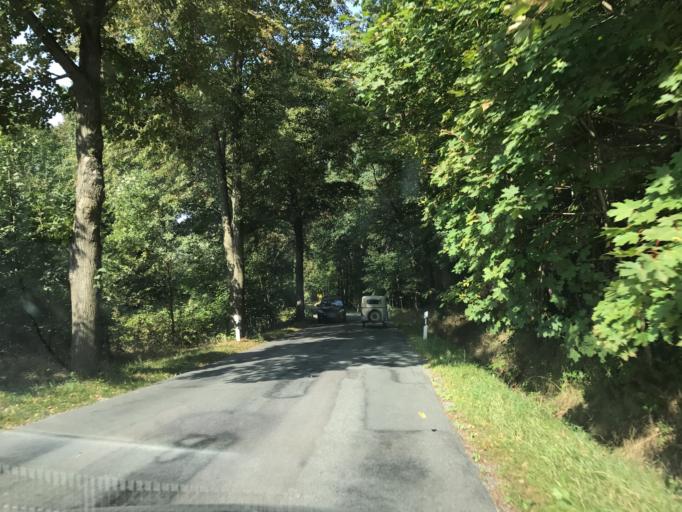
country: DE
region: Saxony
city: Lobau
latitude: 51.0886
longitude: 14.6801
